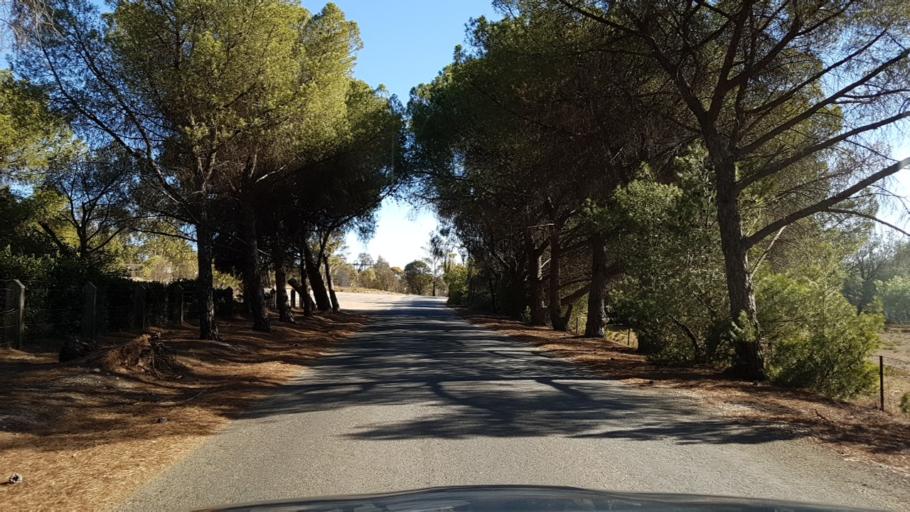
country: AU
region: South Australia
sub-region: Clare and Gilbert Valleys
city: Clare
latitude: -33.6745
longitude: 138.9214
